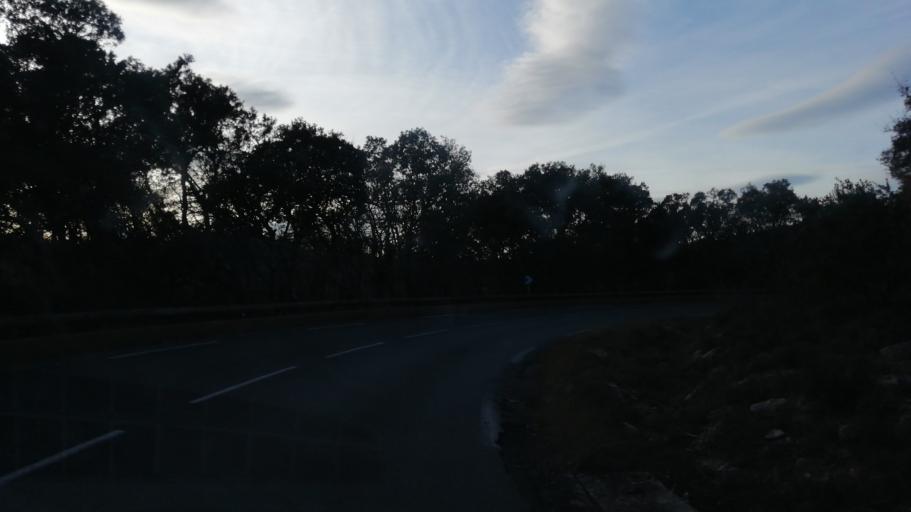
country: FR
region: Languedoc-Roussillon
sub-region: Departement de l'Herault
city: Claret
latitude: 43.8318
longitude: 3.9220
